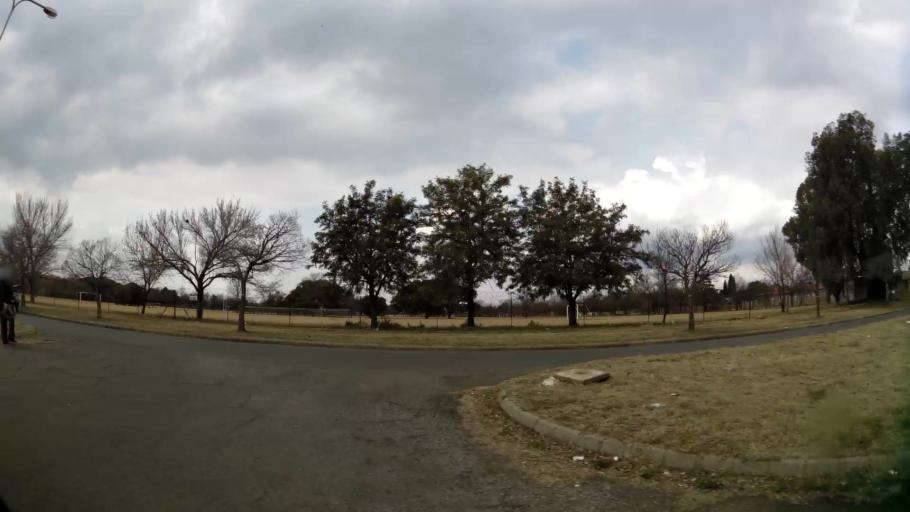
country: ZA
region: Gauteng
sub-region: Sedibeng District Municipality
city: Vanderbijlpark
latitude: -26.7161
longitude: 27.8234
